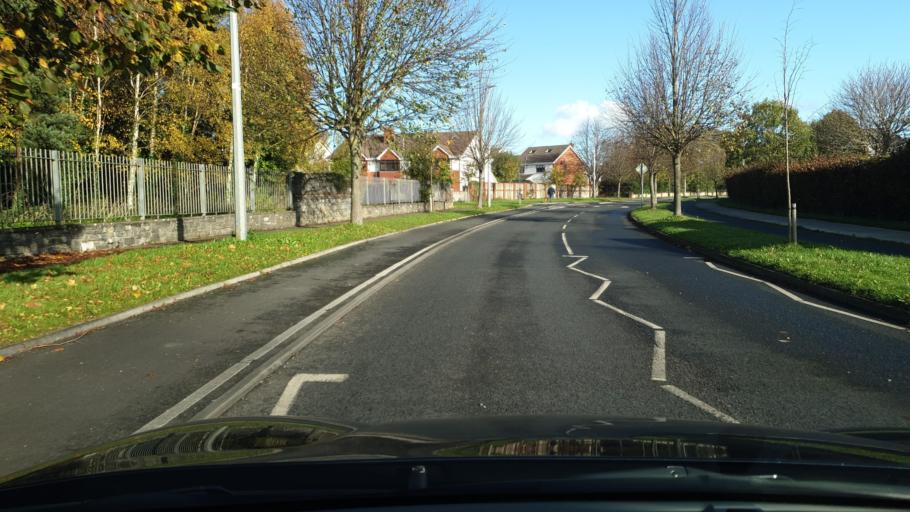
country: IE
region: Leinster
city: Lucan
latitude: 53.3535
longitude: -6.4270
